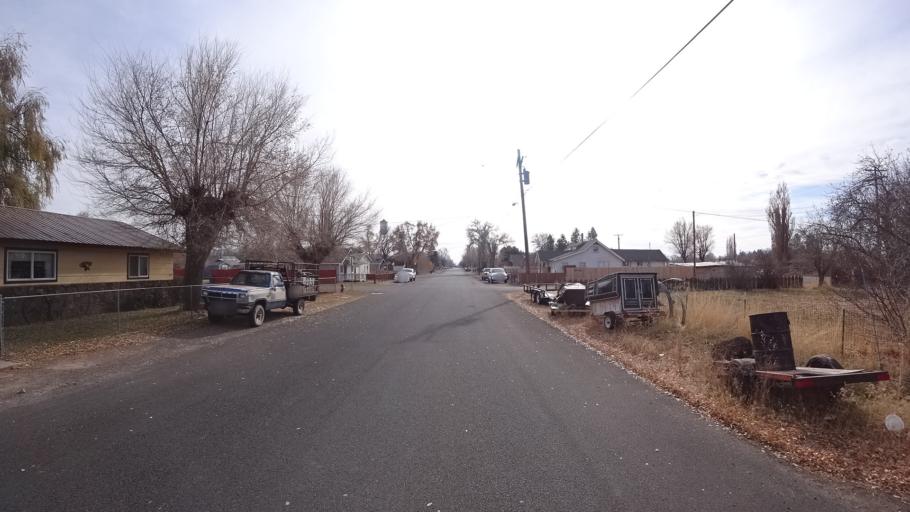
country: US
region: Oregon
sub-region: Klamath County
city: Klamath Falls
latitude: 41.9689
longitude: -121.9208
